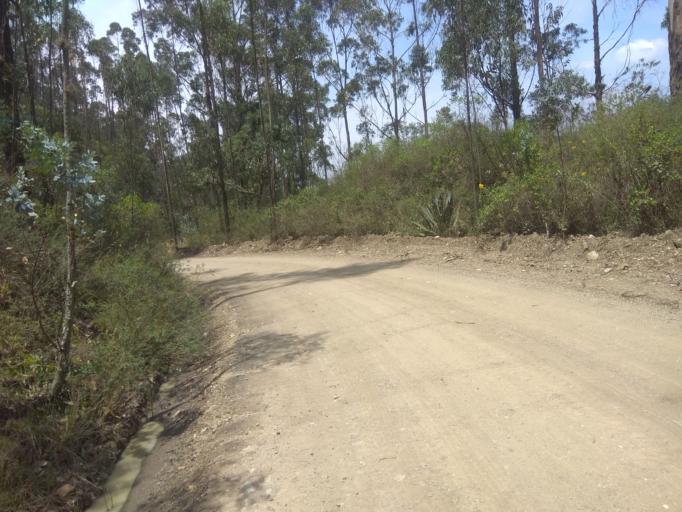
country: CO
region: Boyaca
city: Socha Viejo
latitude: 5.9814
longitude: -72.7331
